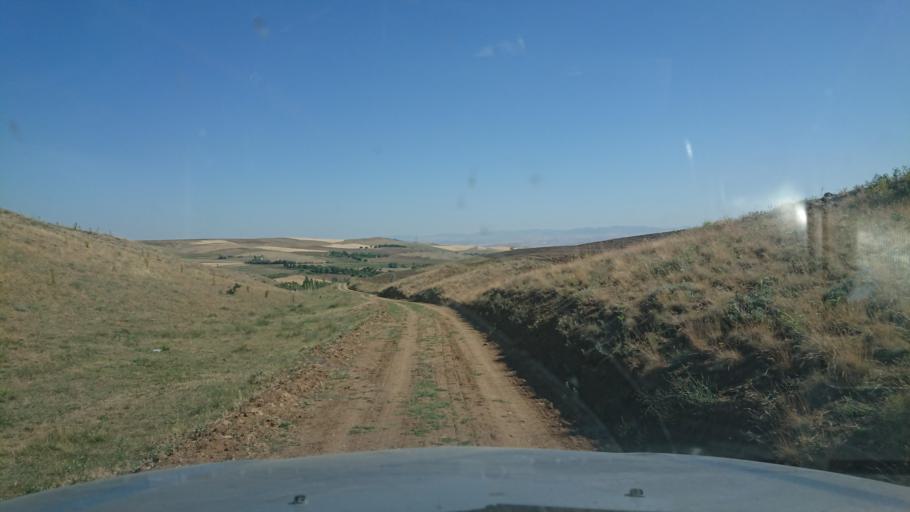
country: TR
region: Aksaray
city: Agacoren
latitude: 38.8358
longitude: 33.9272
